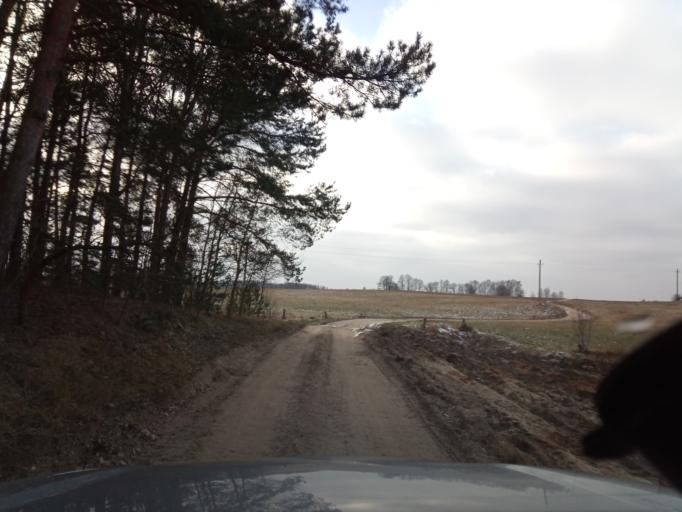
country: LT
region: Alytaus apskritis
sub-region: Alytaus rajonas
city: Daugai
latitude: 54.3759
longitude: 24.3937
